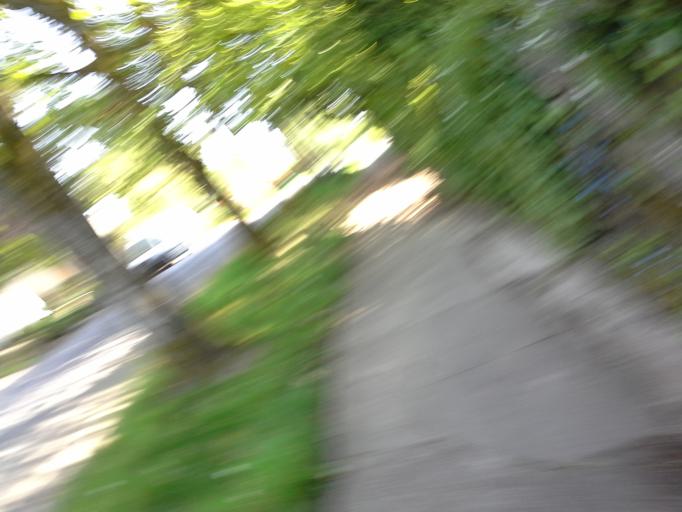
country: US
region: Oregon
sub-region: Clackamas County
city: Milwaukie
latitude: 45.4714
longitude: -122.6765
